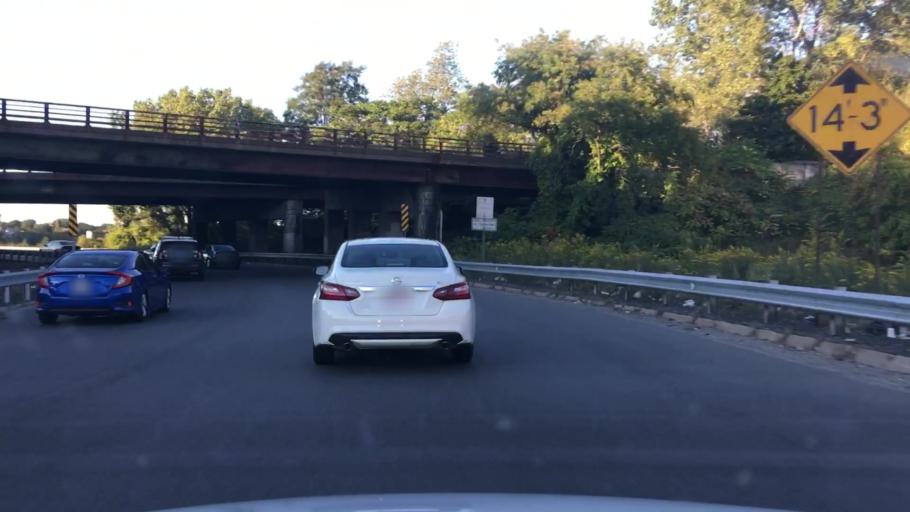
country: US
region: Massachusetts
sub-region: Suffolk County
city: Revere
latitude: 42.4302
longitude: -71.0152
